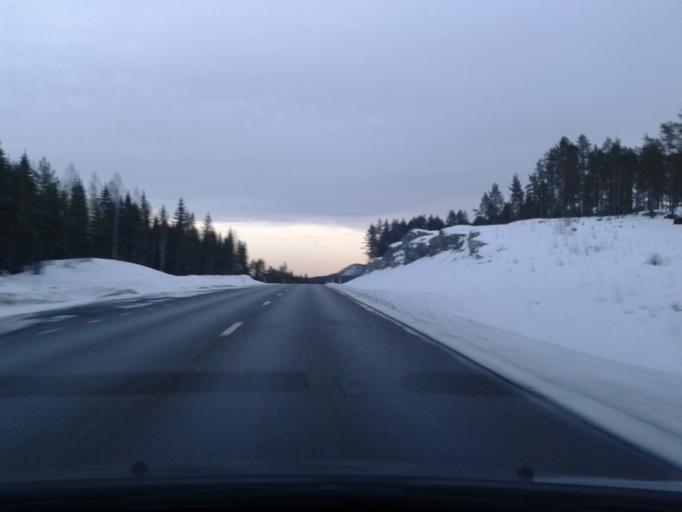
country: SE
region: Vaesternorrland
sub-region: Kramfors Kommun
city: Bollstabruk
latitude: 63.0551
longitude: 17.6134
